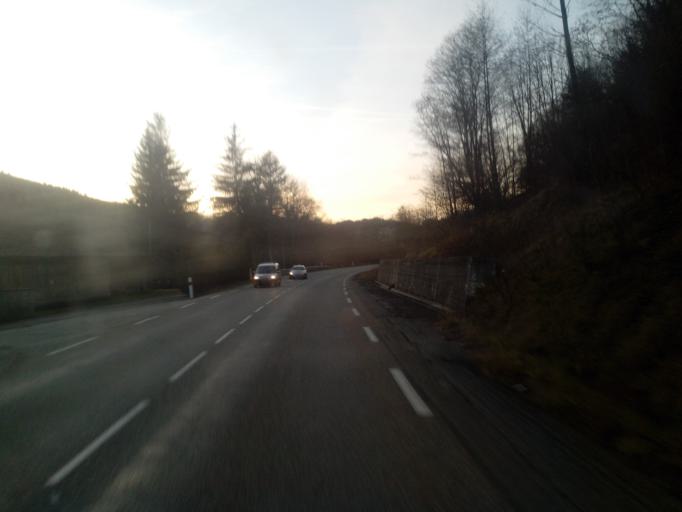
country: FR
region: Midi-Pyrenees
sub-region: Departement de l'Ariege
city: Lavelanet
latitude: 42.9138
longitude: 1.7735
